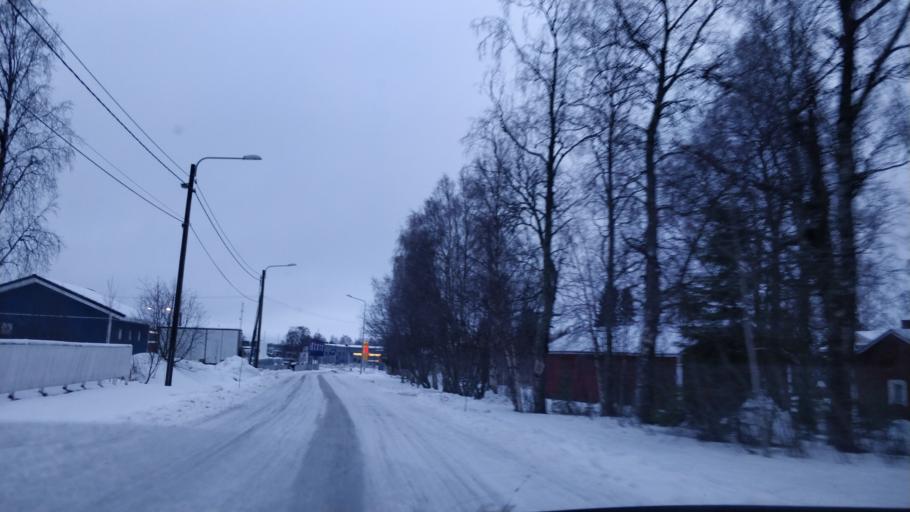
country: FI
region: Lapland
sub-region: Kemi-Tornio
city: Kemi
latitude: 65.7450
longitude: 24.5756
